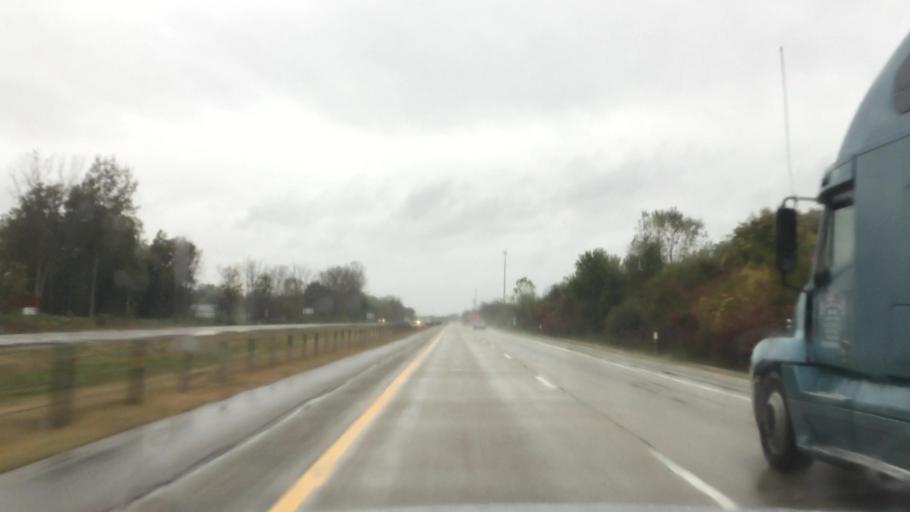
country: US
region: Michigan
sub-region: Van Buren County
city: Hartford
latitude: 42.1911
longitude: -86.1795
